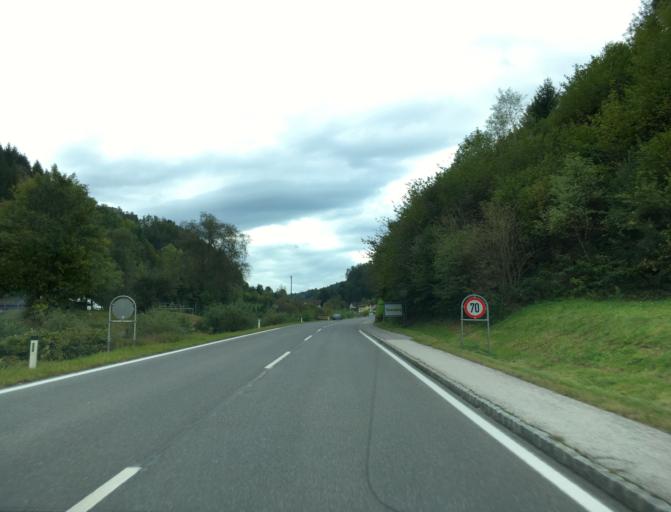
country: AT
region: Lower Austria
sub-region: Politischer Bezirk Neunkirchen
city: Thomasberg
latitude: 47.5733
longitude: 16.1429
